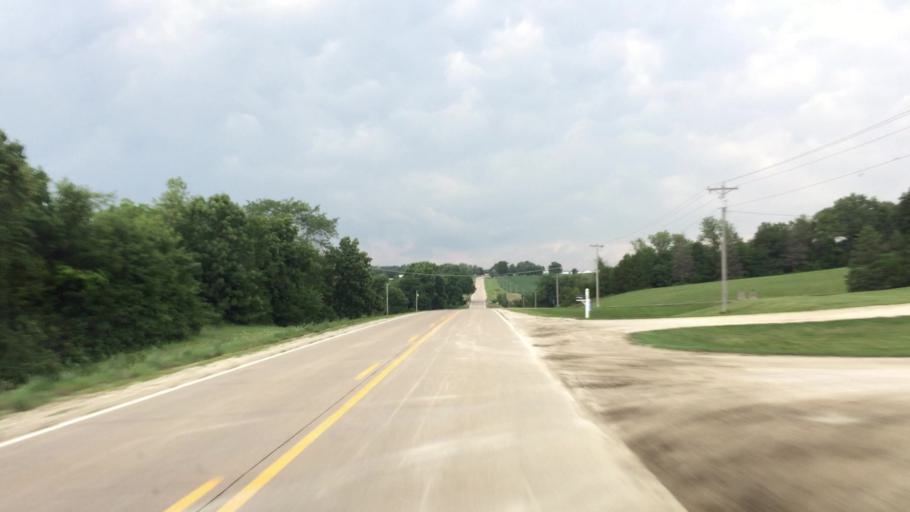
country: US
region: Iowa
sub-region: Lee County
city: Fort Madison
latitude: 40.7199
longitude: -91.3298
